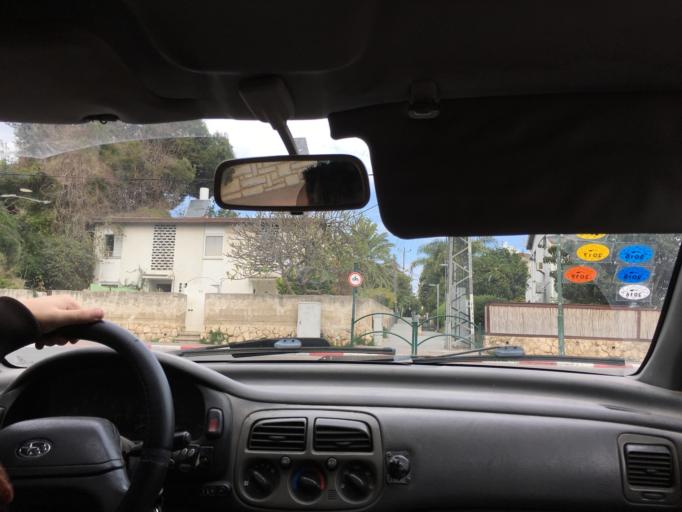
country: IL
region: Tel Aviv
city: Ramat HaSharon
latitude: 32.1354
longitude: 34.8507
